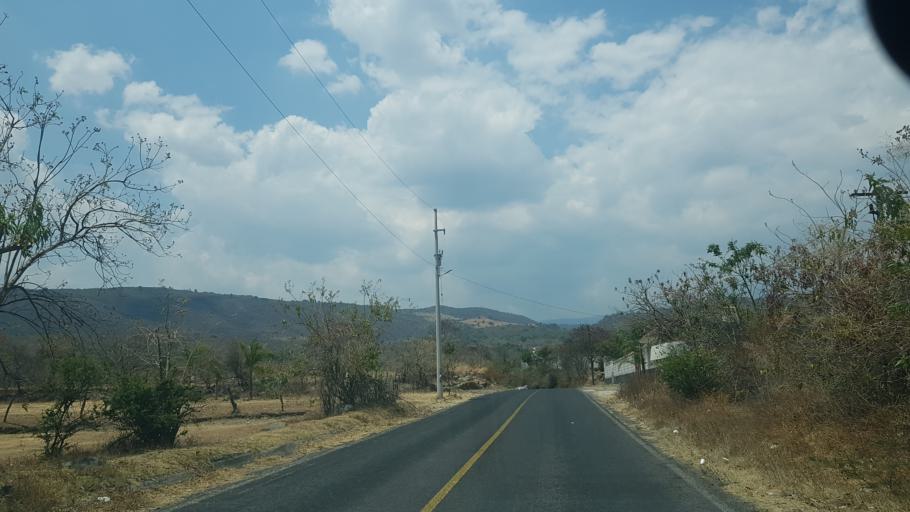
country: MX
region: Puebla
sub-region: Atzitzihuacan
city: Santiago Atzitzihuacan
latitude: 18.8412
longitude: -98.5845
